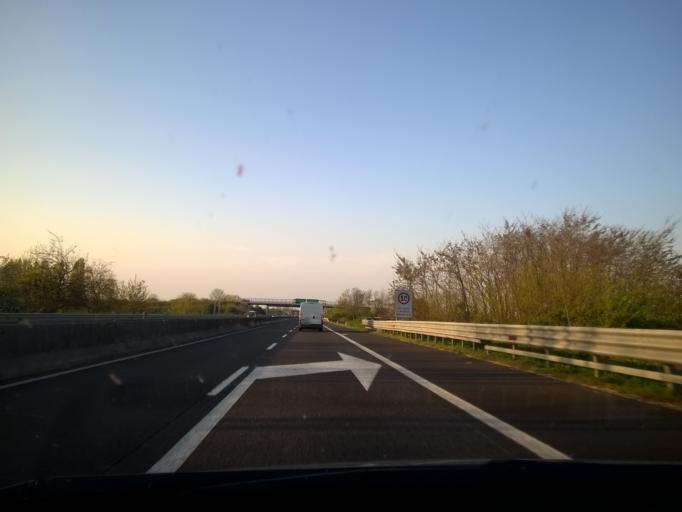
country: IT
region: Emilia-Romagna
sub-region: Provincia di Ferrara
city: Porotto-Cassama
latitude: 44.8617
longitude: 11.5700
